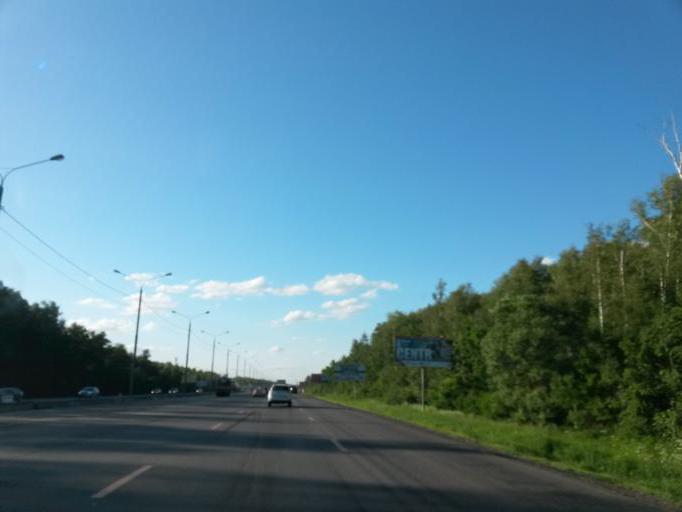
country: RU
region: Moskovskaya
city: Shcherbinka
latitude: 55.4963
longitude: 37.6110
